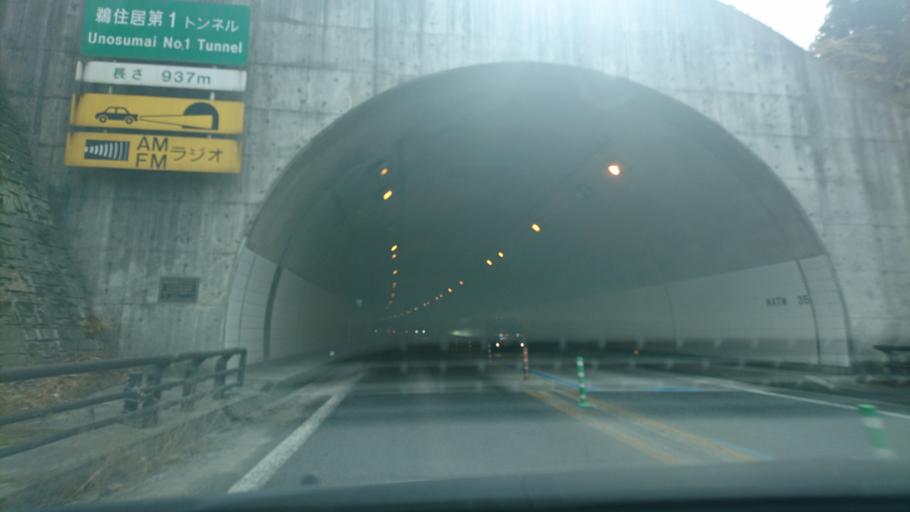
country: JP
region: Iwate
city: Otsuchi
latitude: 39.3331
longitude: 141.8788
